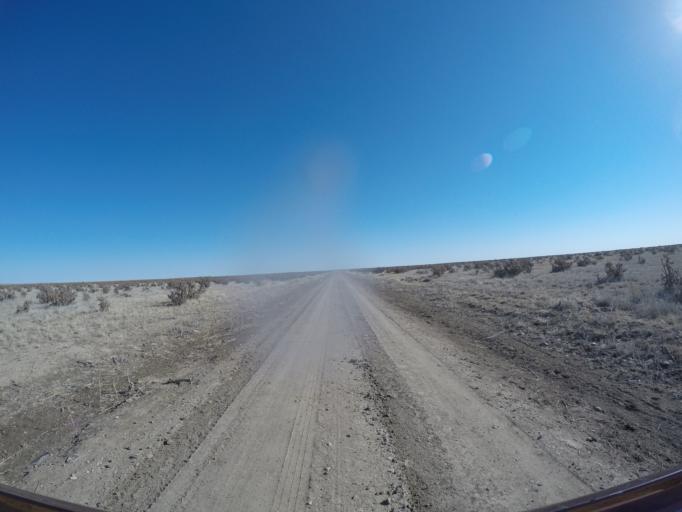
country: US
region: Colorado
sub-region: Otero County
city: La Junta
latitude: 37.6590
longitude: -103.6188
